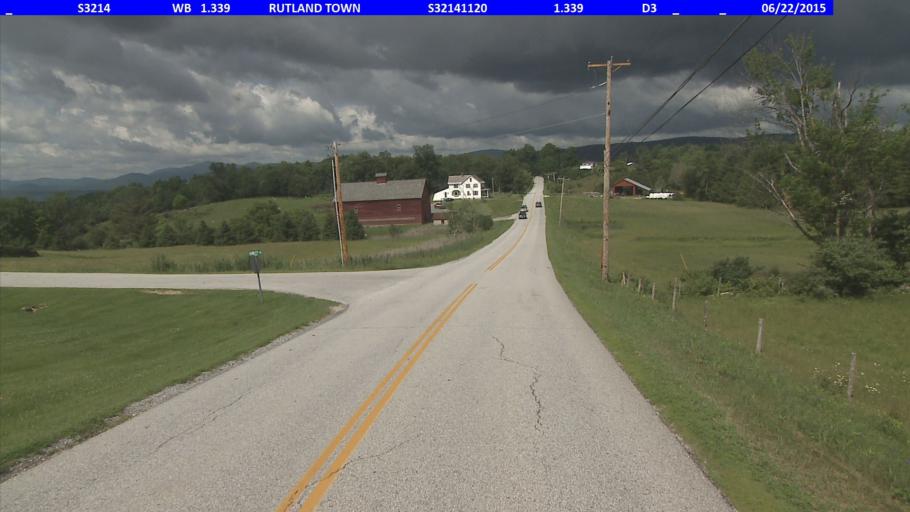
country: US
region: Vermont
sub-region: Rutland County
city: Rutland
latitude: 43.6402
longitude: -72.9520
